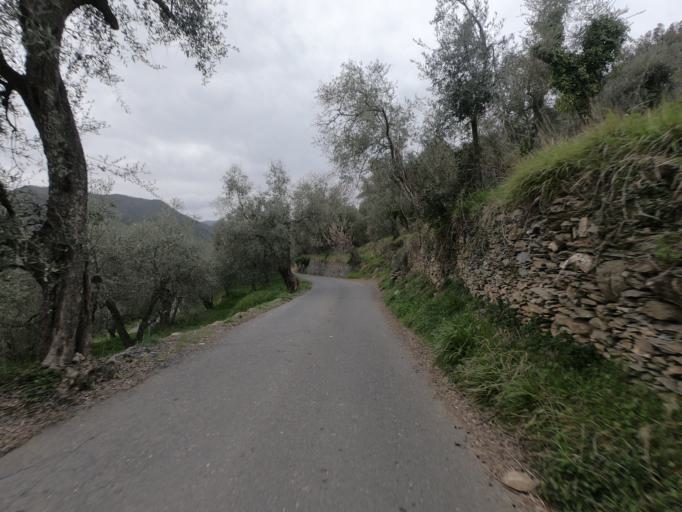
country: IT
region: Liguria
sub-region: Provincia di Savona
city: Casanova Lerrone
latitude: 44.0322
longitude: 8.0455
